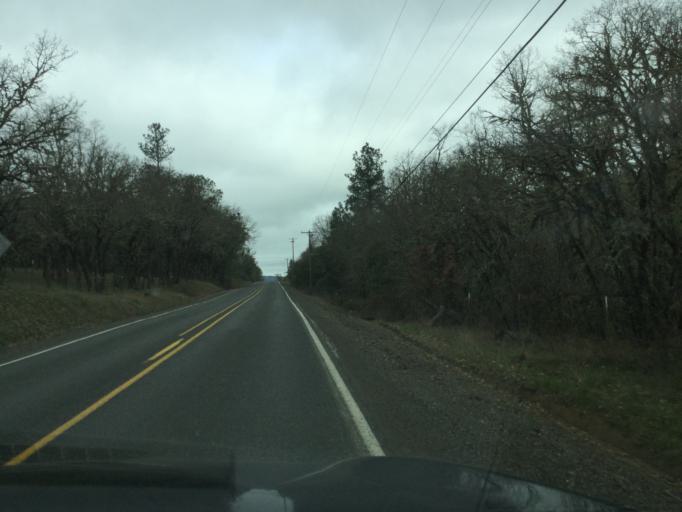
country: US
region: Oregon
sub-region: Jackson County
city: Central Point
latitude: 42.3900
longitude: -122.9872
